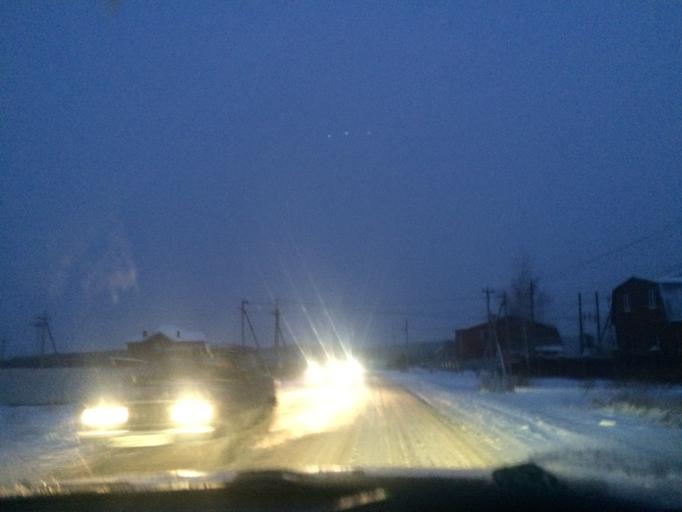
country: RU
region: Tula
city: Barsuki
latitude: 54.1677
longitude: 37.4525
